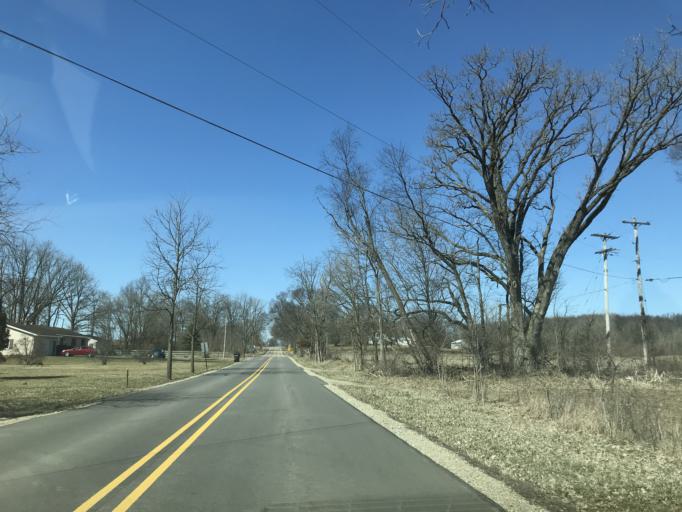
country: US
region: Michigan
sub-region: Hillsdale County
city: Jonesville
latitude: 41.9855
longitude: -84.6788
